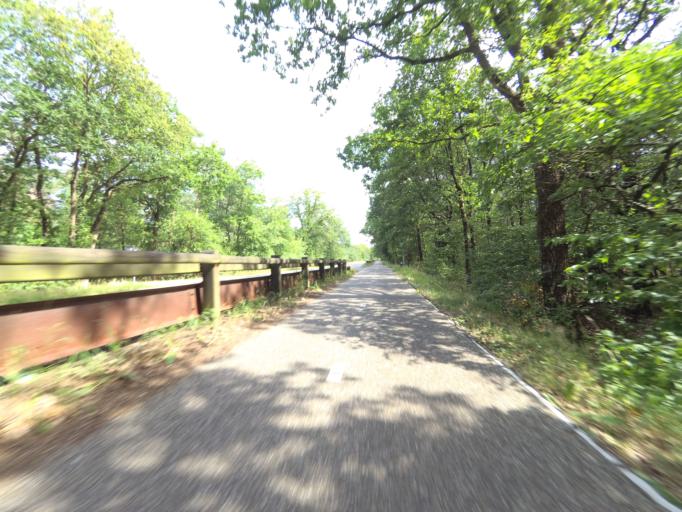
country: NL
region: Gelderland
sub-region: Gemeente Ede
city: Otterlo
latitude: 52.1082
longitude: 5.7772
